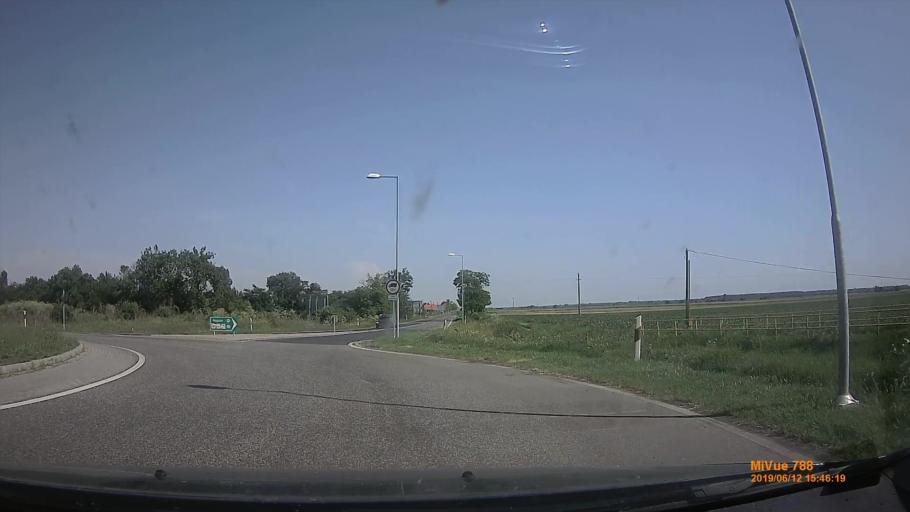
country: HU
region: Csongrad
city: Mako
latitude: 46.2166
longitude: 20.5200
